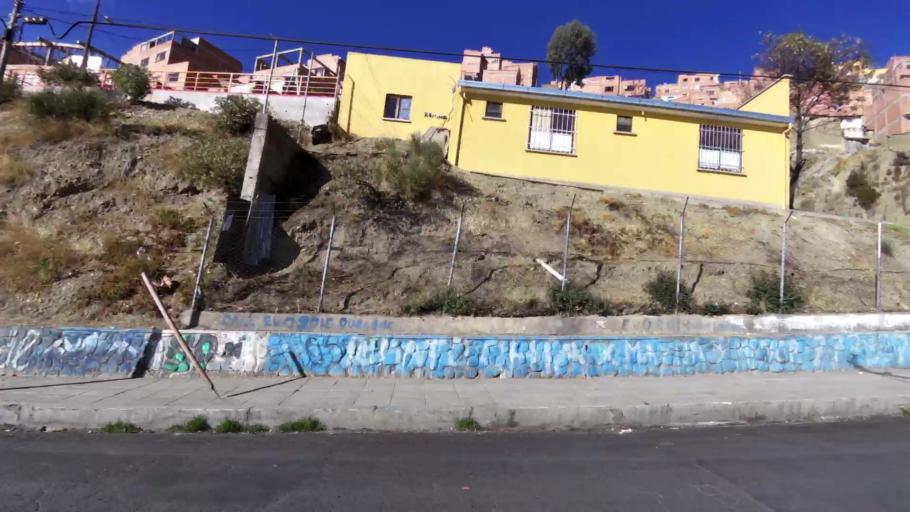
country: BO
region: La Paz
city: La Paz
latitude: -16.5065
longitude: -68.1552
